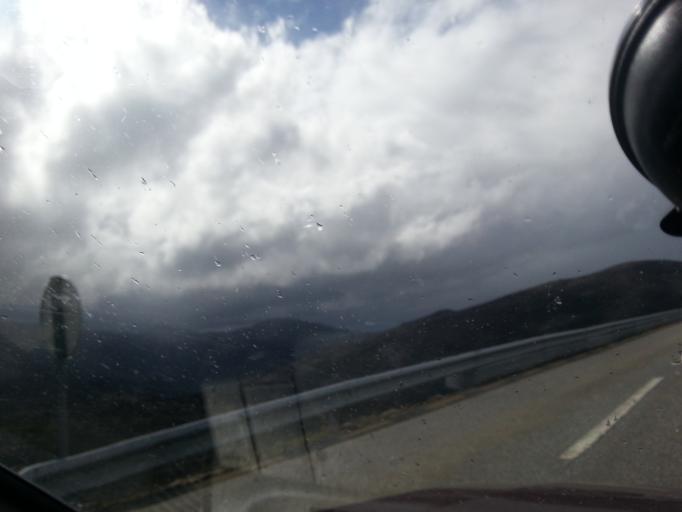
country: PT
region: Guarda
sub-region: Manteigas
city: Manteigas
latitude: 40.4172
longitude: -7.6135
